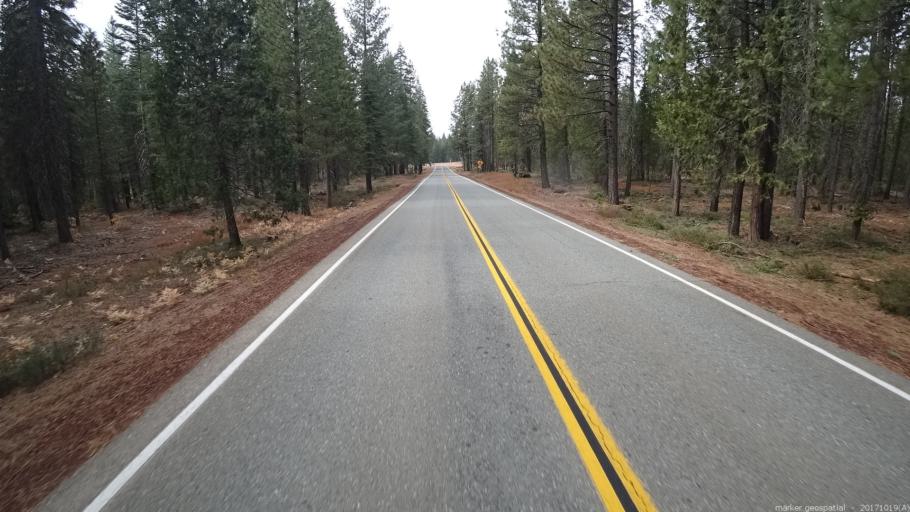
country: US
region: California
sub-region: Shasta County
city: Burney
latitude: 41.1450
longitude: -121.6437
